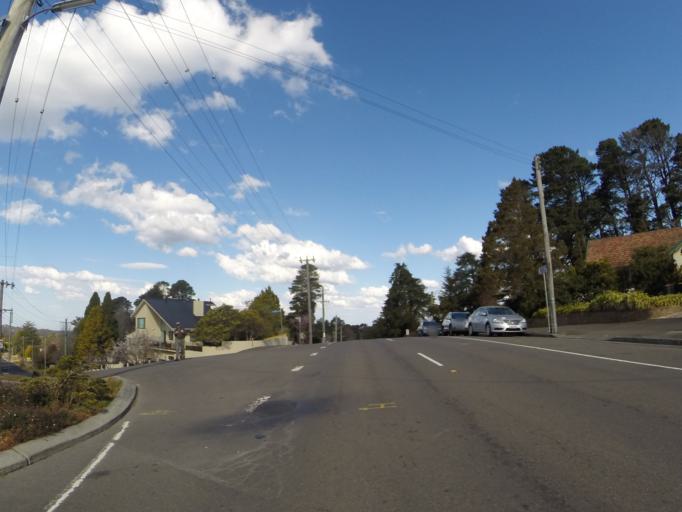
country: AU
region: New South Wales
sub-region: Blue Mountains Municipality
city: Katoomba
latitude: -33.7284
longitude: 150.3108
